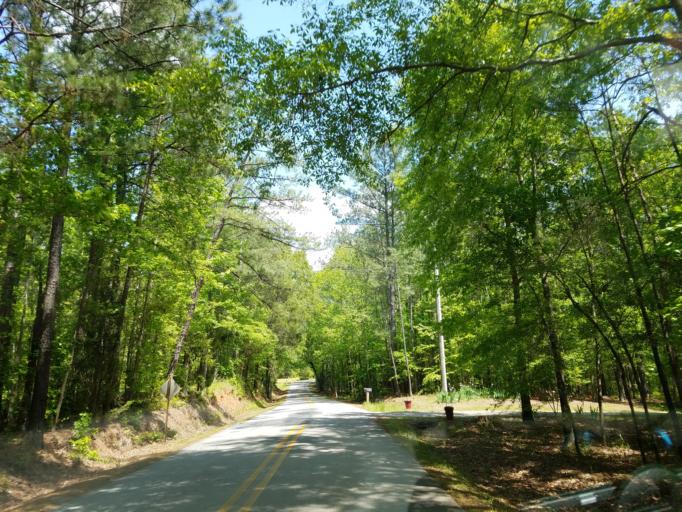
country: US
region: Georgia
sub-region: Monroe County
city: Forsyth
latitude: 33.1398
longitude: -83.9868
